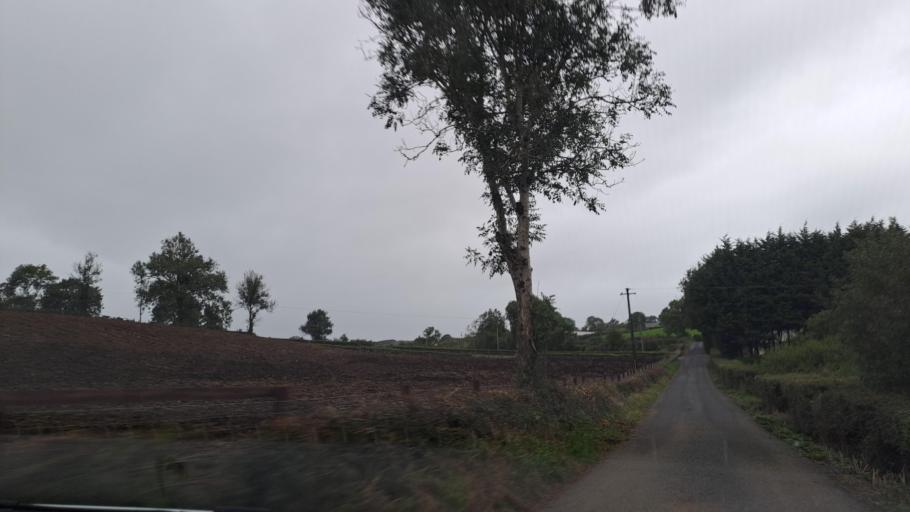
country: IE
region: Ulster
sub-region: An Cabhan
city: Kingscourt
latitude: 54.0008
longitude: -6.8547
